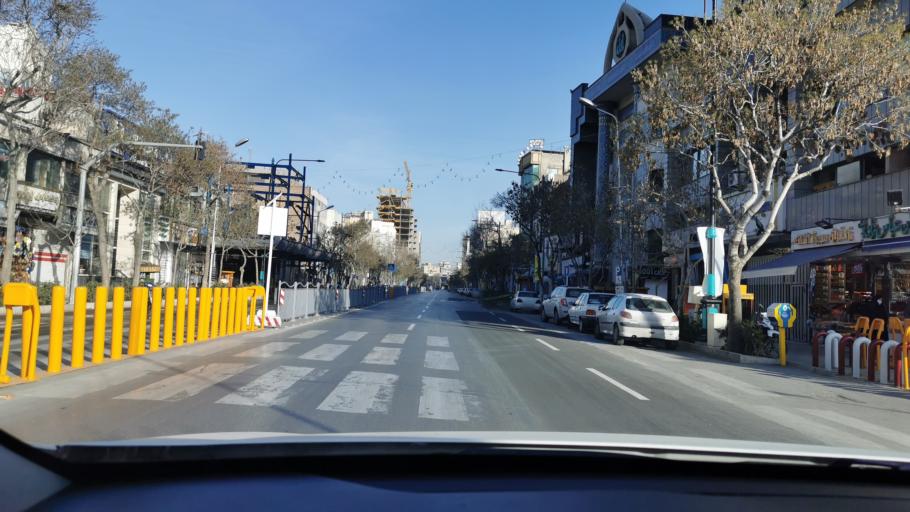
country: IR
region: Razavi Khorasan
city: Mashhad
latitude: 36.2863
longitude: 59.6102
